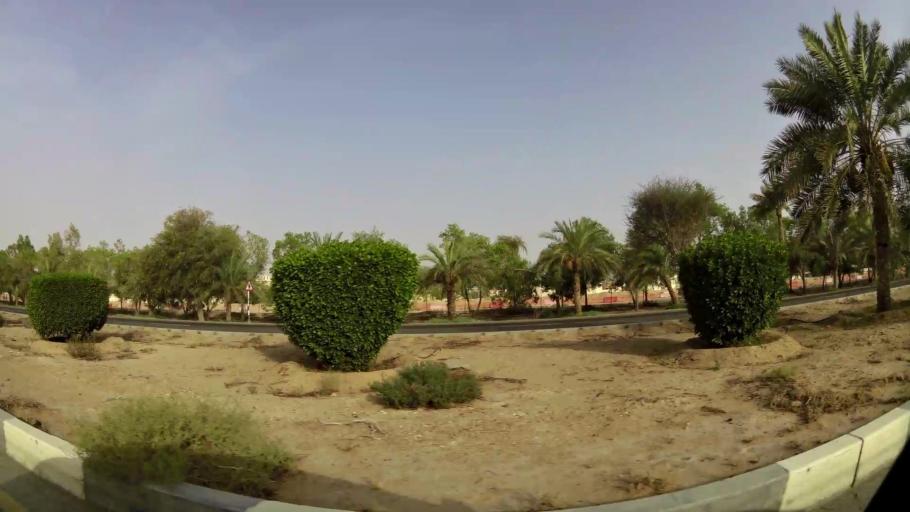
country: AE
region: Abu Dhabi
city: Al Ain
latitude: 24.1265
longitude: 55.7071
